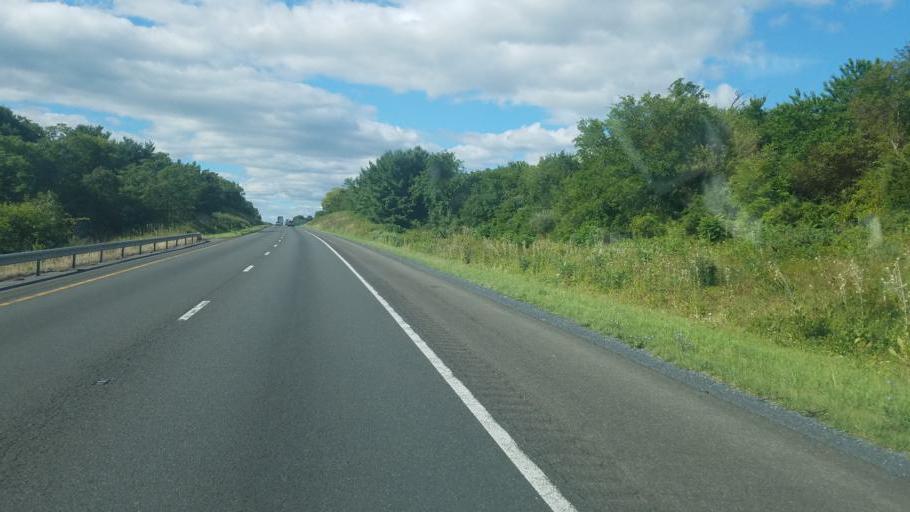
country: US
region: Virginia
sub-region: Frederick County
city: Stephens City
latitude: 39.1049
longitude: -78.2029
